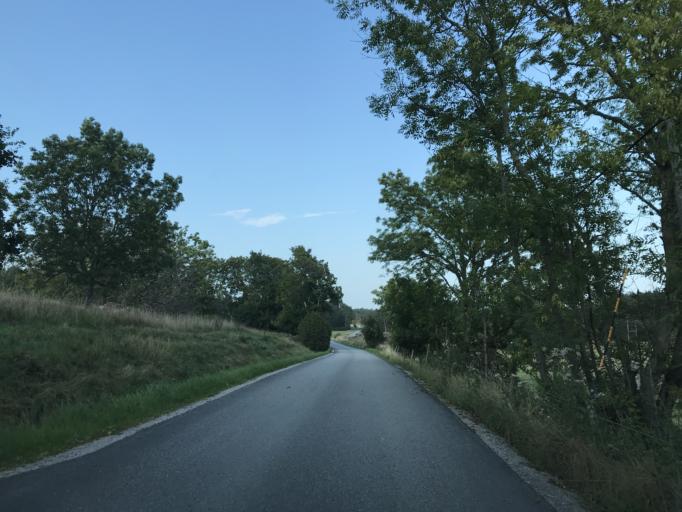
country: SE
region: Stockholm
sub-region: Norrtalje Kommun
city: Bjorko
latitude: 59.8512
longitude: 19.0126
